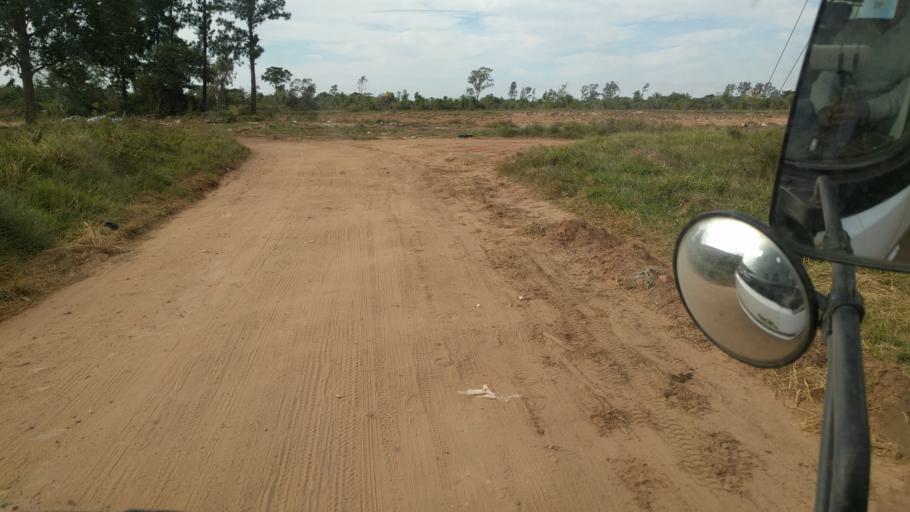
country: BO
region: Santa Cruz
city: Santa Cruz de la Sierra
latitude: -17.6822
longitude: -63.1429
